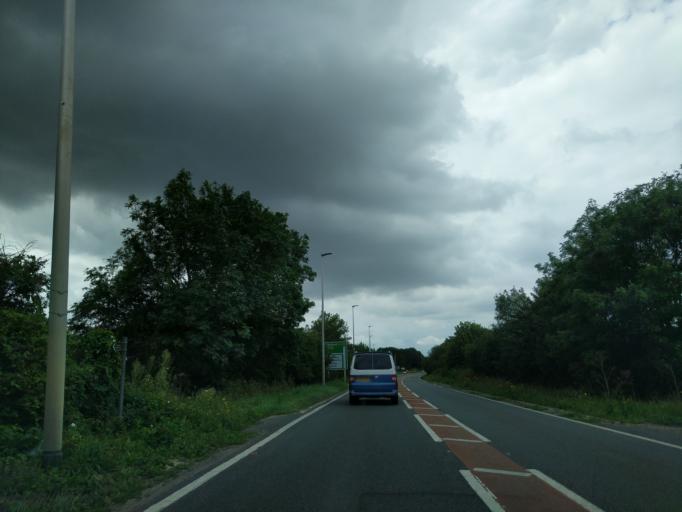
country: GB
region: England
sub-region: Cambridgeshire
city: Papworth Everard
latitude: 52.2224
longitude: -0.1434
